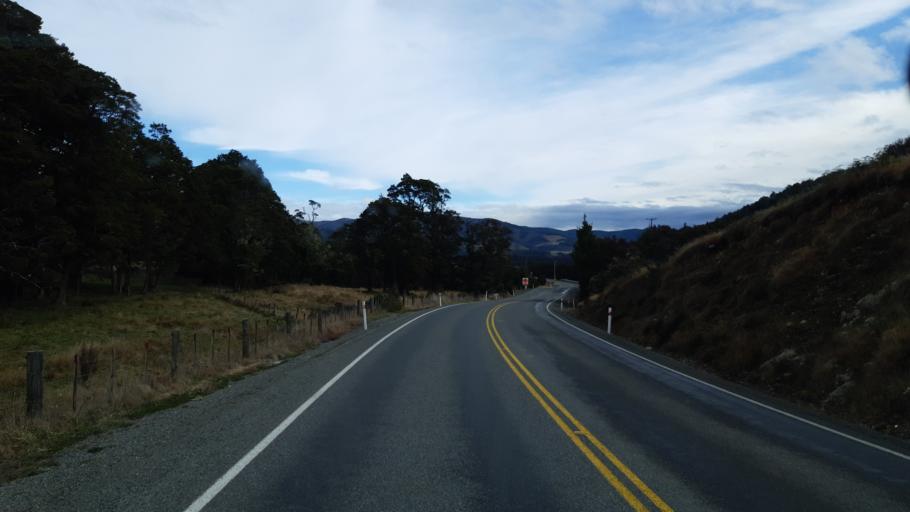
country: NZ
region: Tasman
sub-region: Tasman District
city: Wakefield
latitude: -41.7998
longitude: 172.8645
